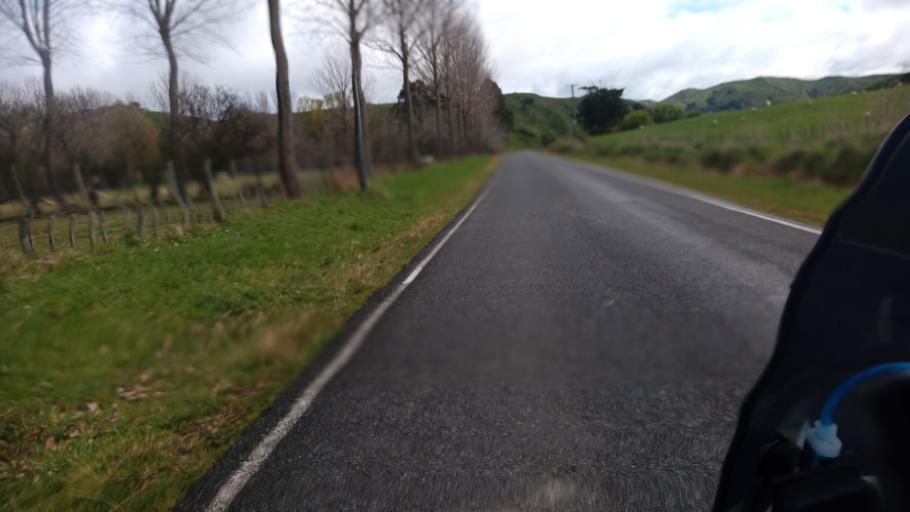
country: NZ
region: Gisborne
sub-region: Gisborne District
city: Gisborne
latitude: -38.5776
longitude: 178.1756
